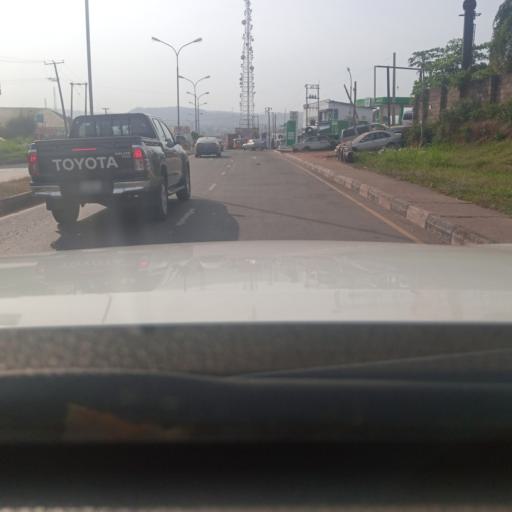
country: NG
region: Enugu
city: Enugu
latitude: 6.4412
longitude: 7.5109
